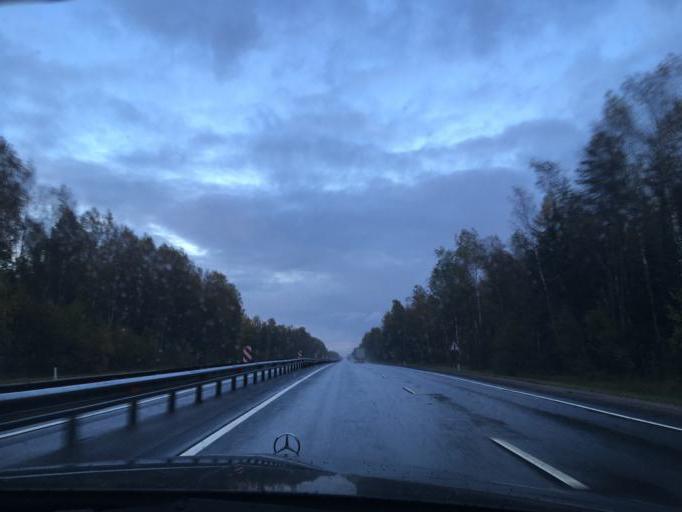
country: RU
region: Smolensk
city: Yartsevo
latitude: 55.0882
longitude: 32.8091
